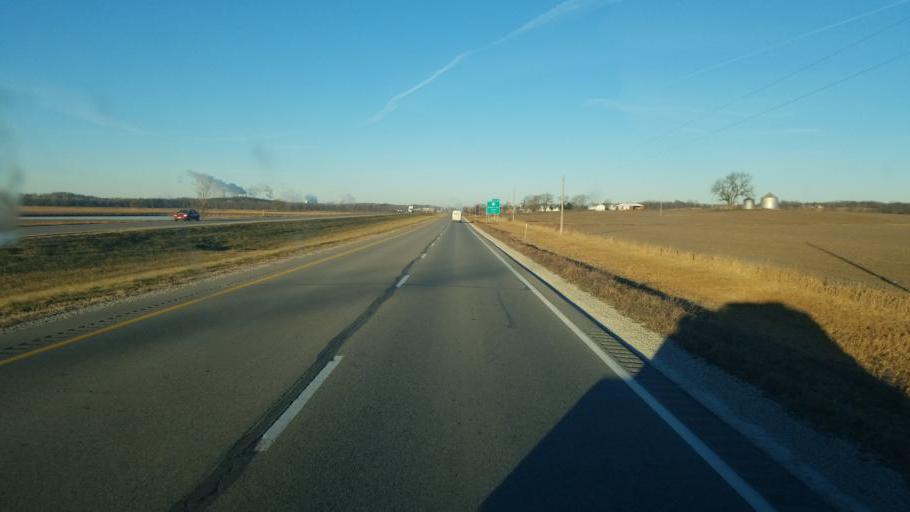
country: US
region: Iowa
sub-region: Wapello County
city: Eddyville
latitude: 41.1388
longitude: -92.5950
